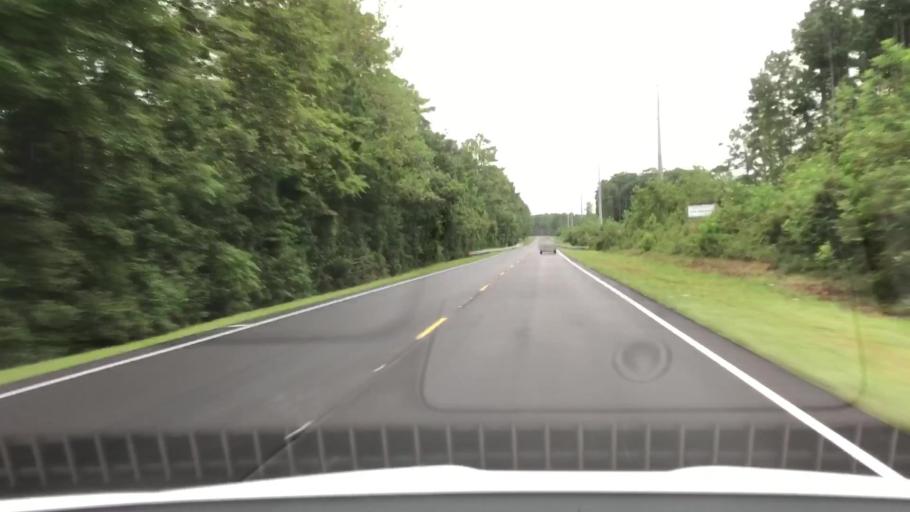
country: US
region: North Carolina
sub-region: Carteret County
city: Cape Carteret
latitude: 34.7644
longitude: -77.0958
